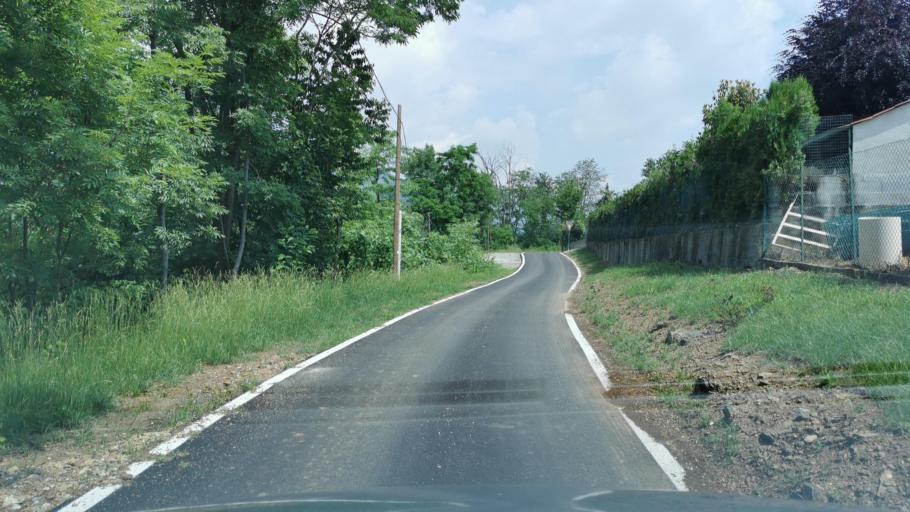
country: IT
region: Piedmont
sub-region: Provincia di Torino
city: Vallo Torinese
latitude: 45.2109
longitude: 7.5002
